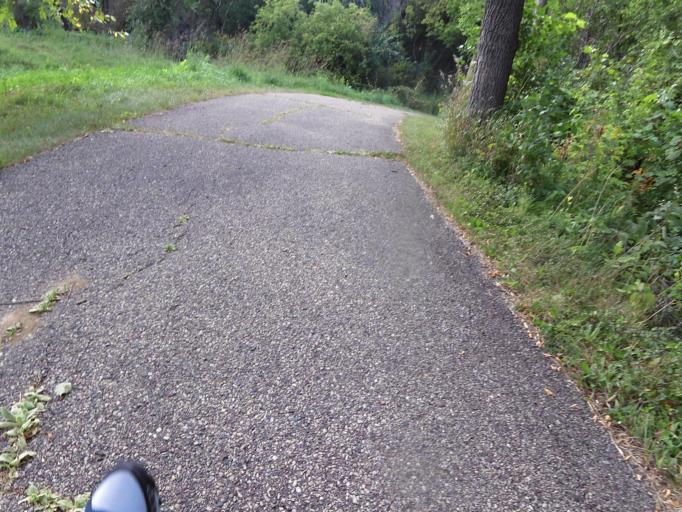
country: US
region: Minnesota
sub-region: Scott County
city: Prior Lake
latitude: 44.7075
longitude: -93.4434
